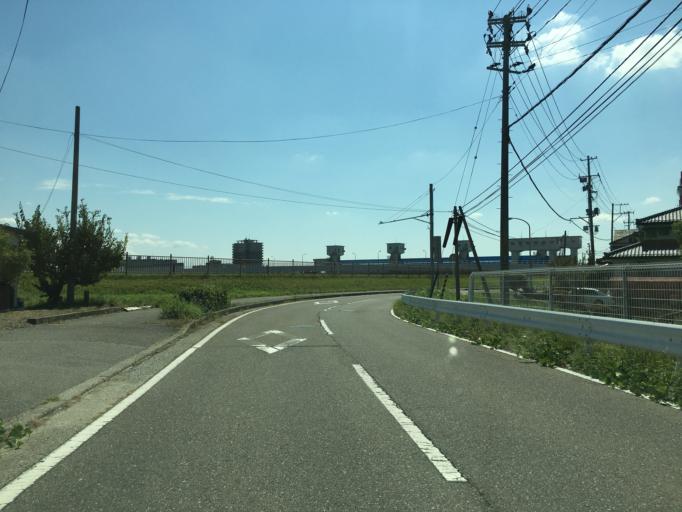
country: JP
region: Niigata
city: Niigata-shi
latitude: 37.8993
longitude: 139.0133
